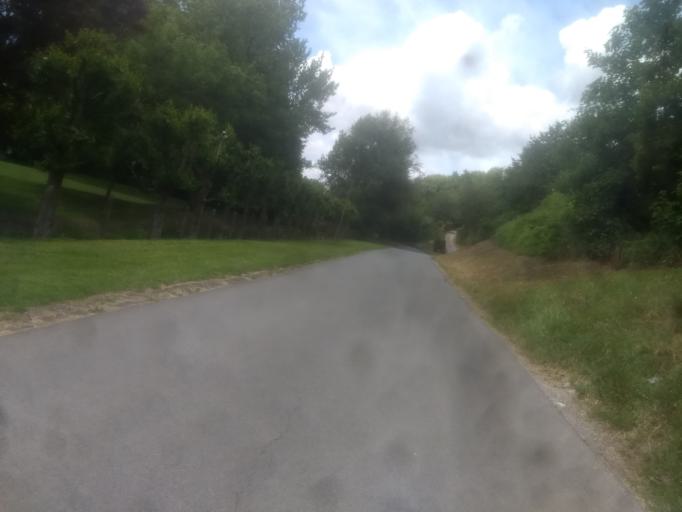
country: FR
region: Nord-Pas-de-Calais
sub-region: Departement du Pas-de-Calais
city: Mont-Saint-Eloi
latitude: 50.3400
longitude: 2.6908
